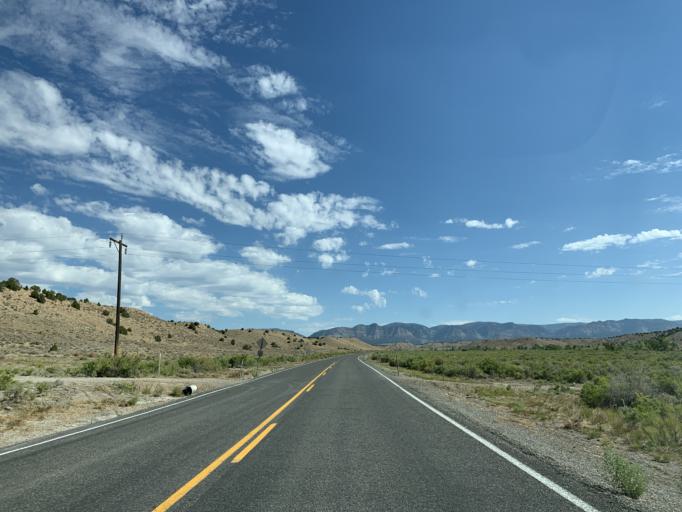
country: US
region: Utah
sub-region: Carbon County
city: Wellington
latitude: 39.5836
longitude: -110.6485
